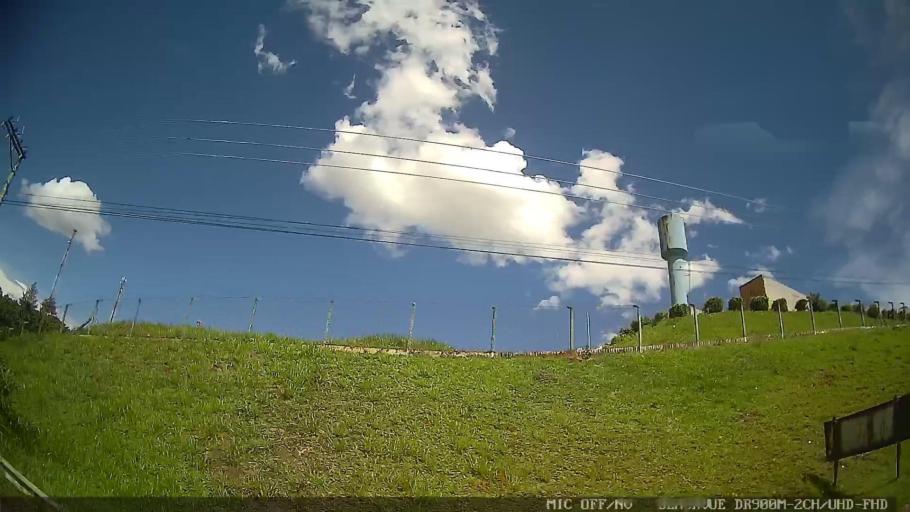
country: BR
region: Sao Paulo
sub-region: Pedreira
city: Pedreira
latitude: -22.7125
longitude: -46.8396
